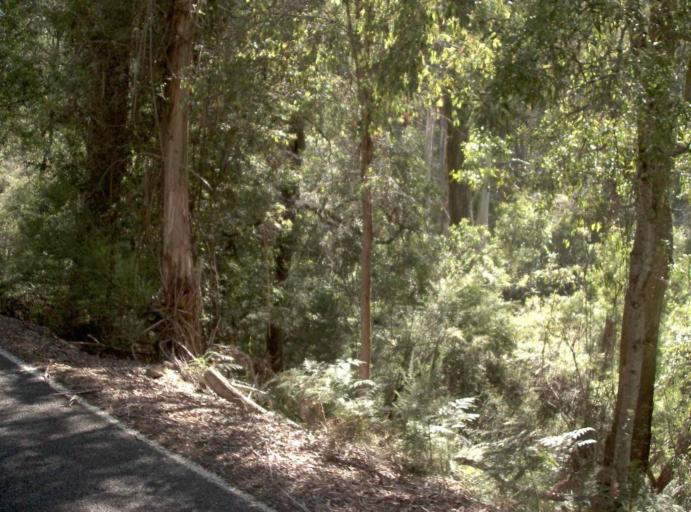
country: AU
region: New South Wales
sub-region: Bombala
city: Bombala
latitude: -37.3766
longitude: 148.6813
